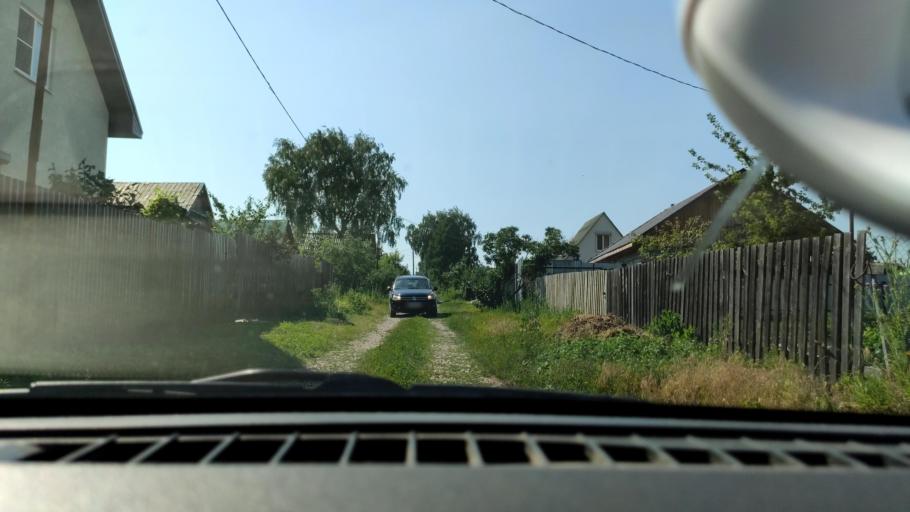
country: RU
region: Samara
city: Petra-Dubrava
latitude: 53.2681
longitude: 50.3004
